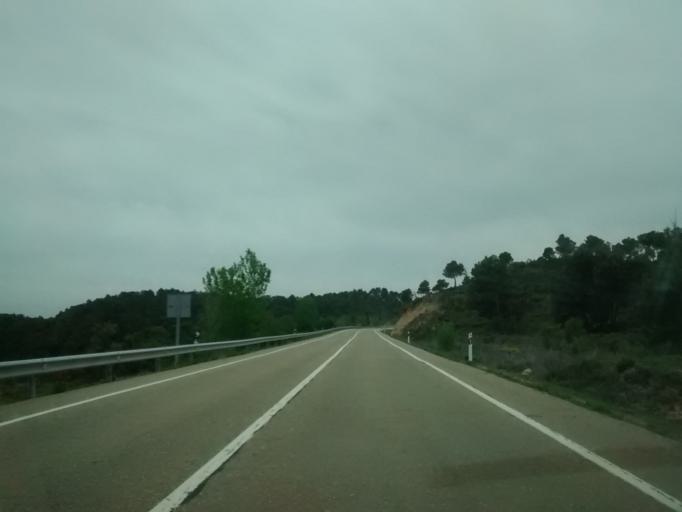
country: ES
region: Aragon
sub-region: Provincia de Teruel
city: Fornoles
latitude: 40.8864
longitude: -0.0312
